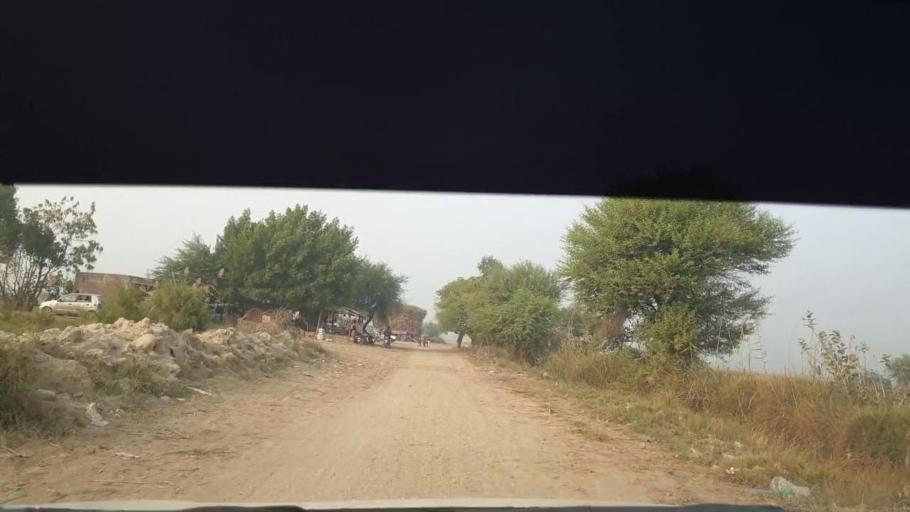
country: PK
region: Sindh
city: Berani
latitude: 25.8413
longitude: 68.8909
